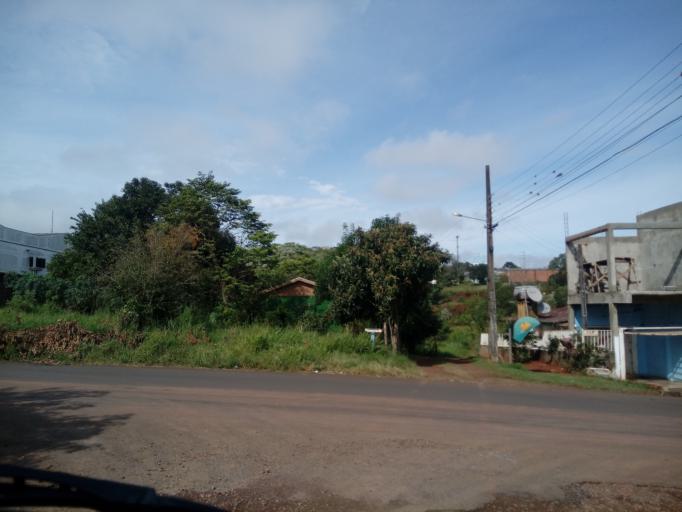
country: BR
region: Santa Catarina
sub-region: Chapeco
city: Chapeco
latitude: -27.0857
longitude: -52.6041
